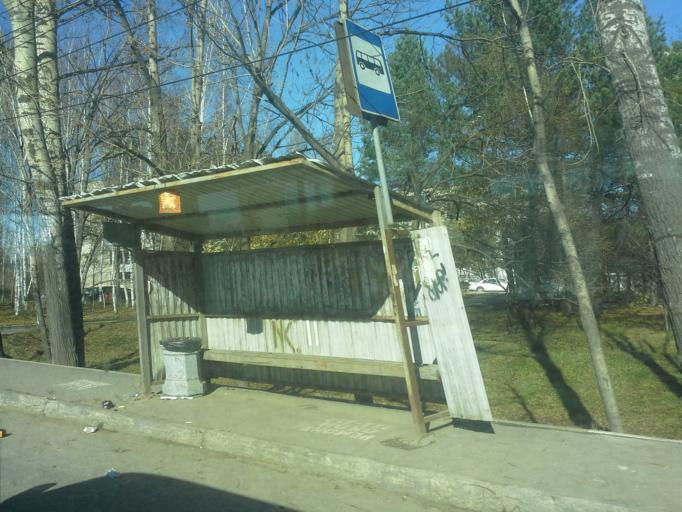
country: RU
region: Khabarovsk Krai
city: Topolevo
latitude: 48.4791
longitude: 135.1539
